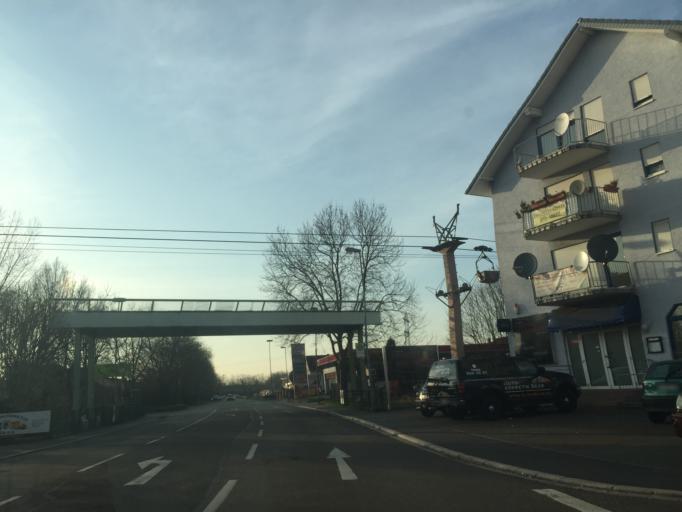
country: DE
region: Baden-Wuerttemberg
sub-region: Karlsruhe Region
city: Leimen
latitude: 49.3512
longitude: 8.6876
